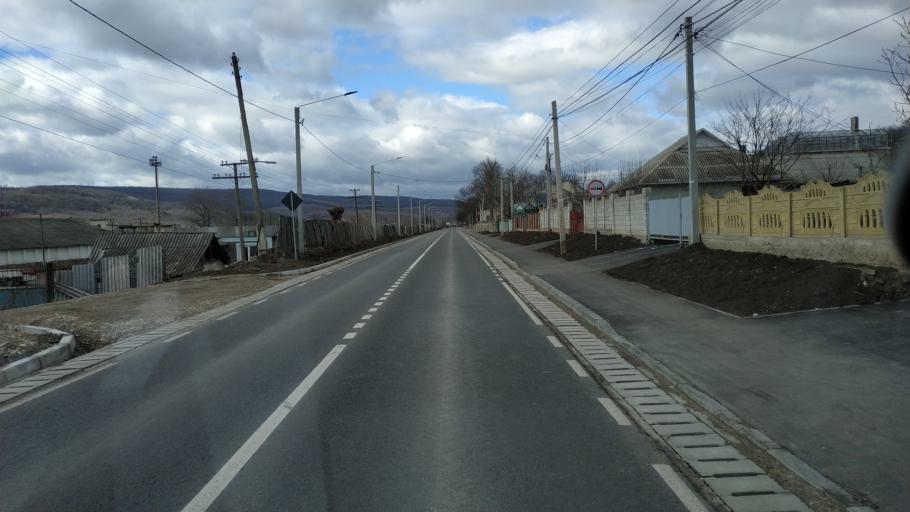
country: MD
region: Stinga Nistrului
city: Bucovat
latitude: 47.1885
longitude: 28.4546
